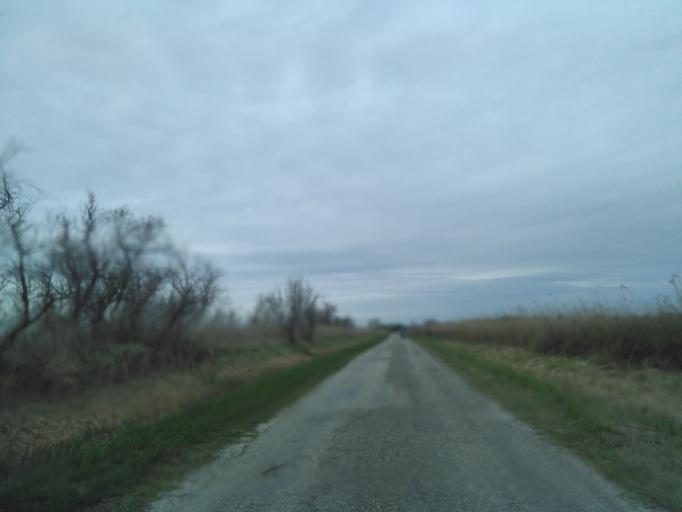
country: FR
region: Provence-Alpes-Cote d'Azur
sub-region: Departement des Bouches-du-Rhone
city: Arles
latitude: 43.5753
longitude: 4.5444
